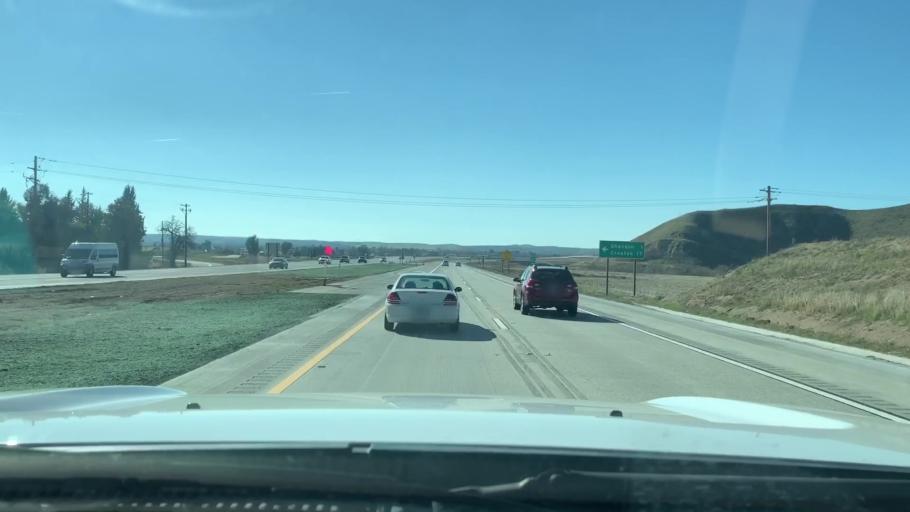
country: US
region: California
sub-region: San Luis Obispo County
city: Shandon
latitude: 35.6681
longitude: -120.3586
